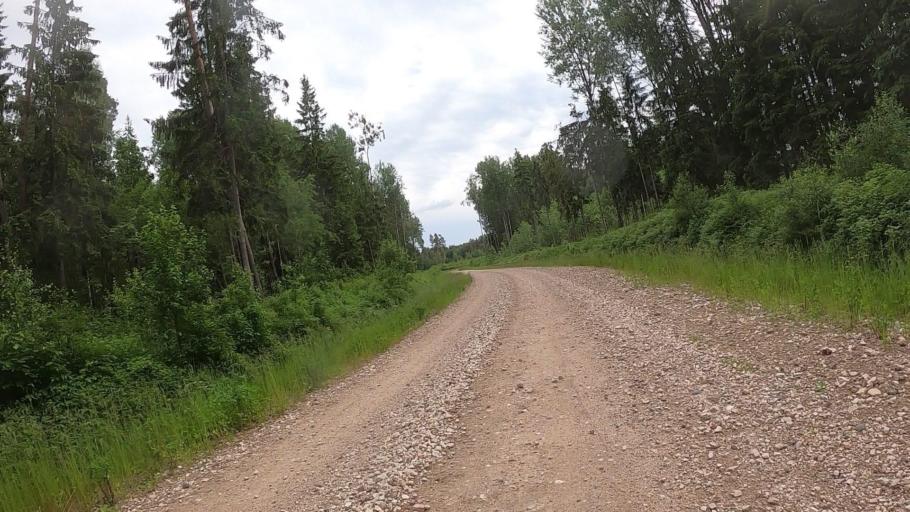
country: LV
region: Olaine
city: Olaine
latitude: 56.7599
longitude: 23.8798
